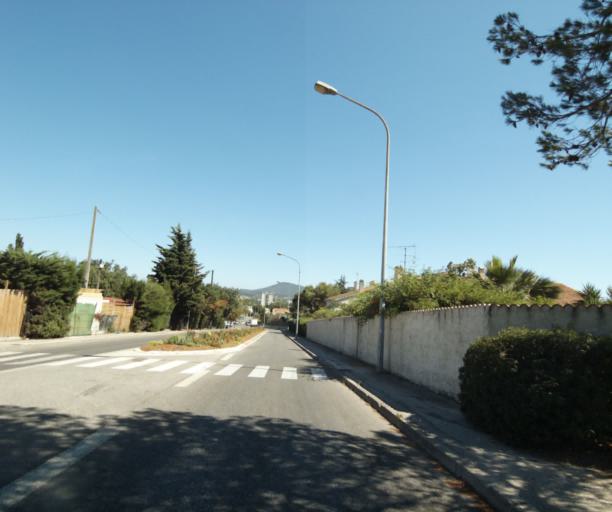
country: FR
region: Provence-Alpes-Cote d'Azur
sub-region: Departement du Var
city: La Garde
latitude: 43.1325
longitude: 6.0091
